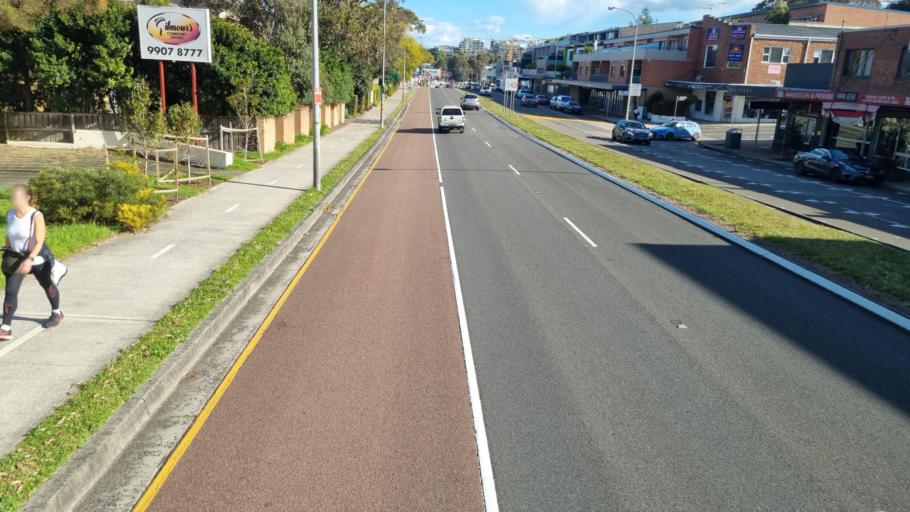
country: AU
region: New South Wales
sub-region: Warringah
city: North Manly
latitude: -33.7835
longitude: 151.2675
